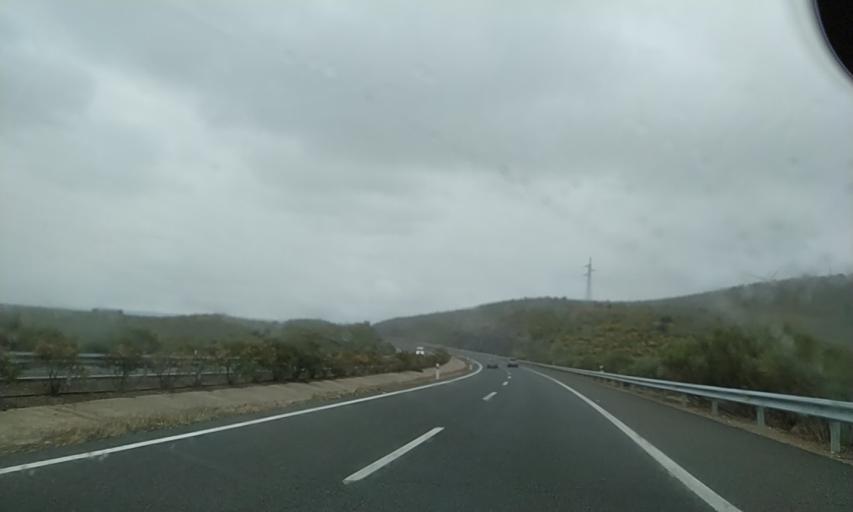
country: ES
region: Extremadura
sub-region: Provincia de Caceres
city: Plasencia
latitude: 40.0057
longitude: -6.1408
